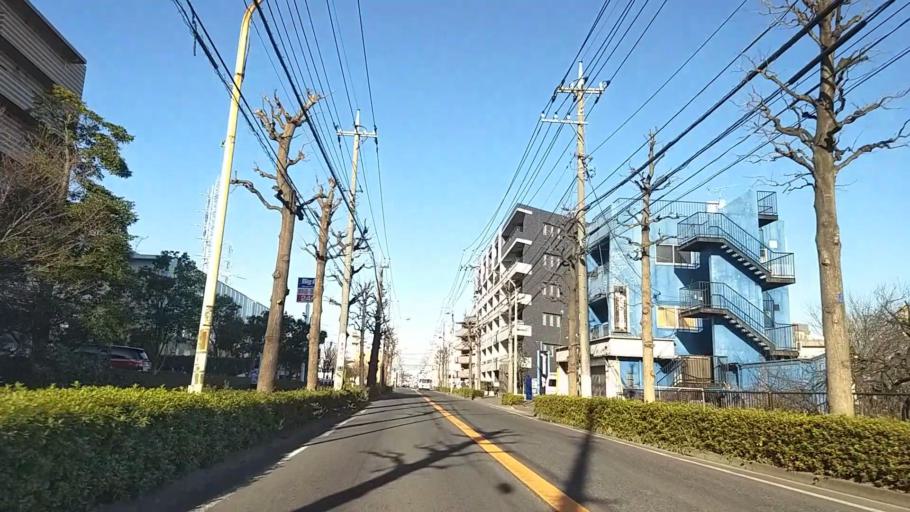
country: JP
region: Tokyo
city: Chofugaoka
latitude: 35.6094
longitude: 139.6049
